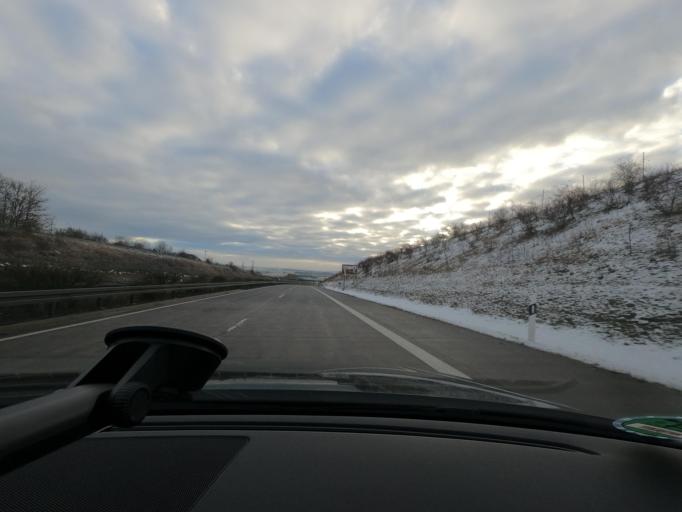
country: DE
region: Thuringia
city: Veilsdorf
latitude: 50.4646
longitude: 10.8407
